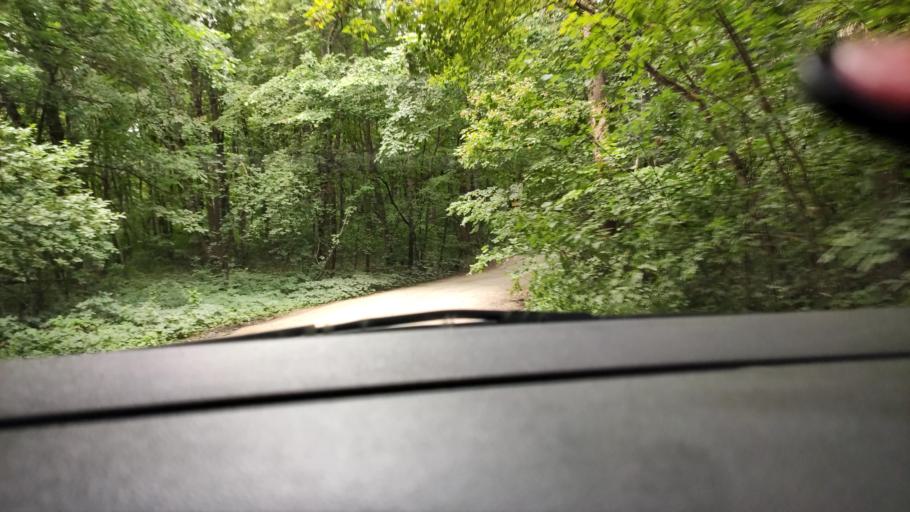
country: RU
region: Voronezj
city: Ramon'
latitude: 51.8895
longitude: 39.3520
